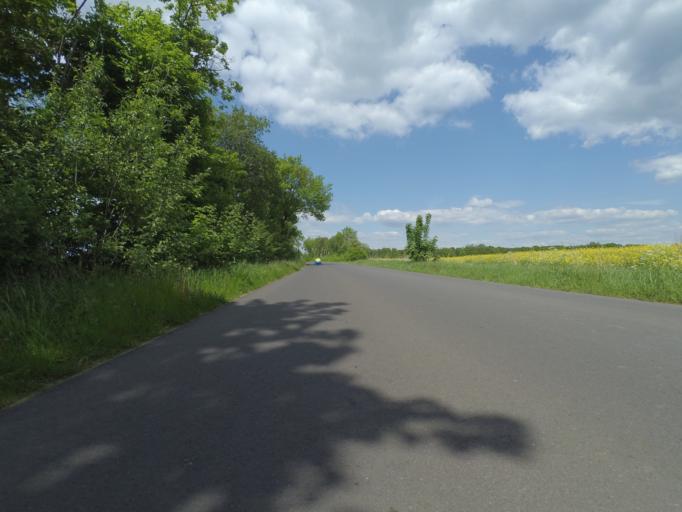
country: DE
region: Lower Saxony
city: Muden
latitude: 52.5073
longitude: 10.3678
